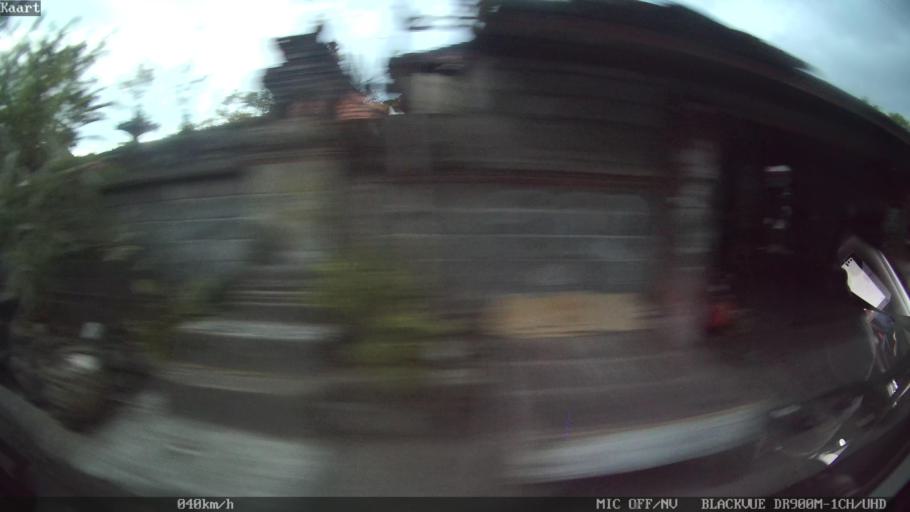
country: ID
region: Bali
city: Banjar Kertajiwa
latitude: -8.6391
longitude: 115.2731
